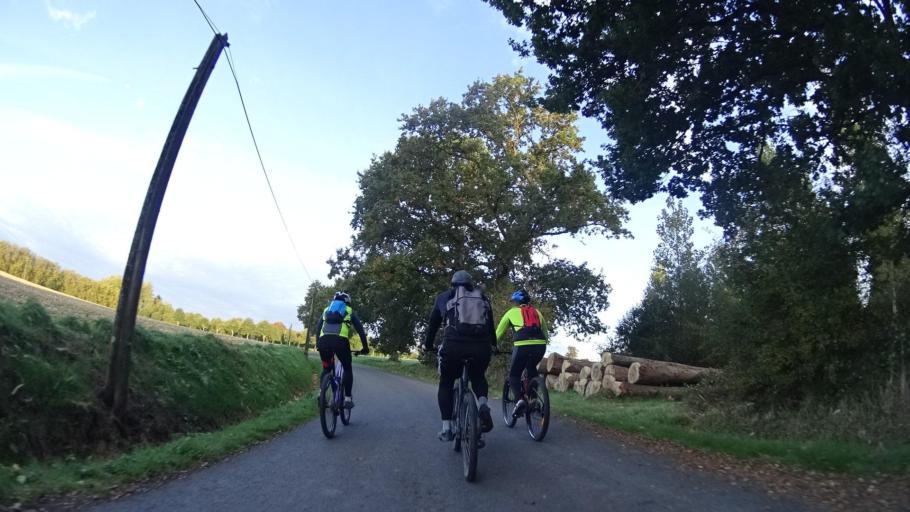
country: FR
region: Brittany
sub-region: Departement des Cotes-d'Armor
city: Evran
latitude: 48.3528
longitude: -1.9410
